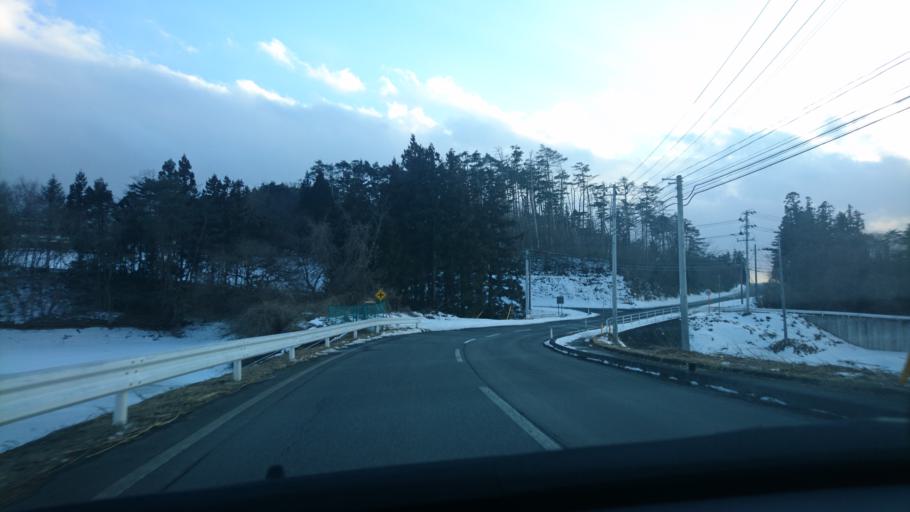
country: JP
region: Iwate
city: Ichinoseki
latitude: 39.0094
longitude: 141.3364
